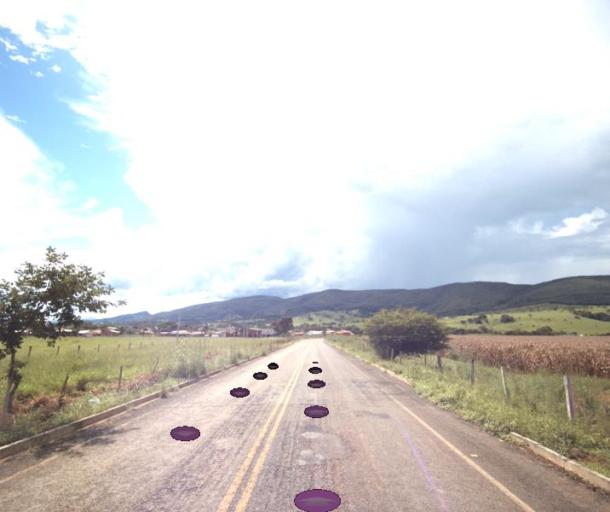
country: BR
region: Goias
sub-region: Pirenopolis
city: Pirenopolis
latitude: -16.0239
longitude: -49.1099
